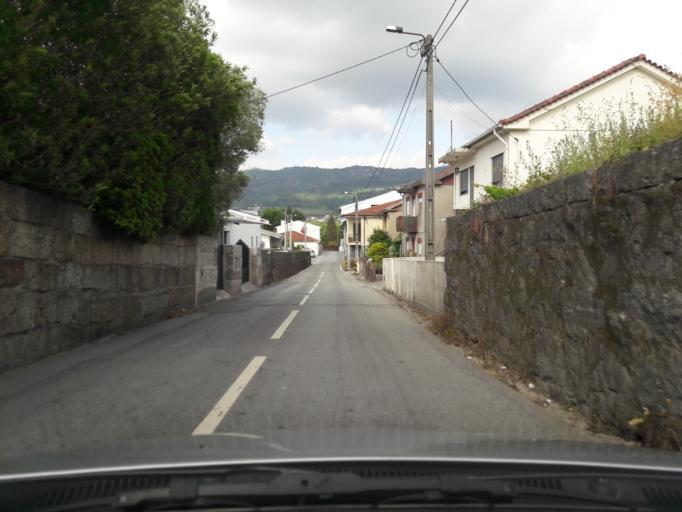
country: PT
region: Braga
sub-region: Guimaraes
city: Urgeses
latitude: 41.4196
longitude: -8.3068
